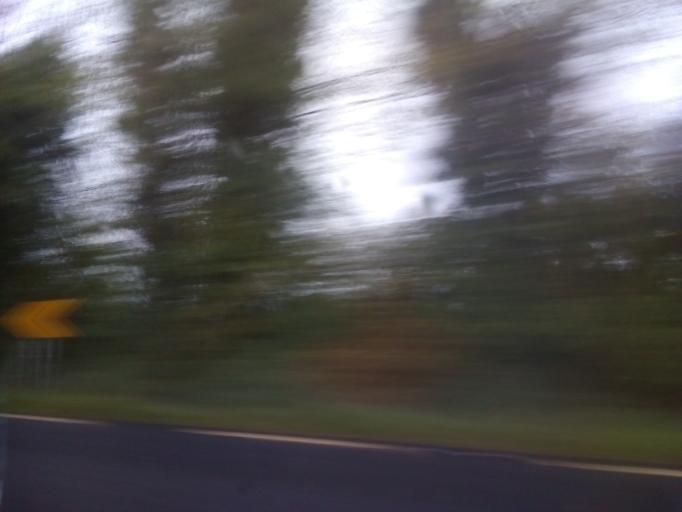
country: IE
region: Connaught
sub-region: Roscommon
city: Roscommon
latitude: 53.7736
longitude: -8.1380
